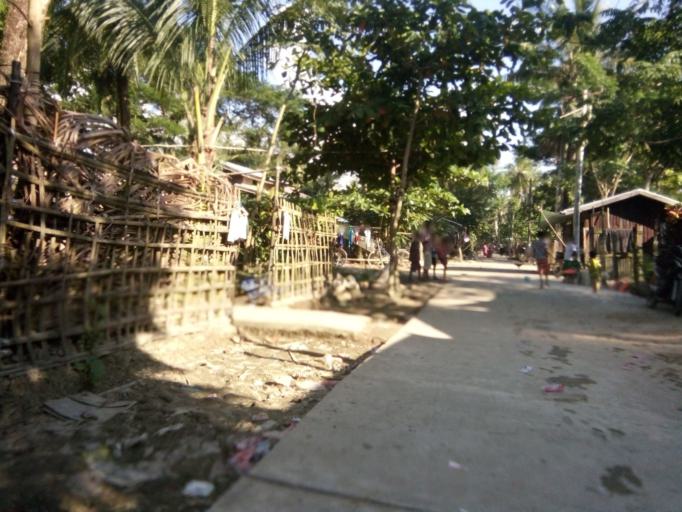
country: MM
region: Yangon
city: Kanbe
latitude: 16.8747
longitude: 95.9782
